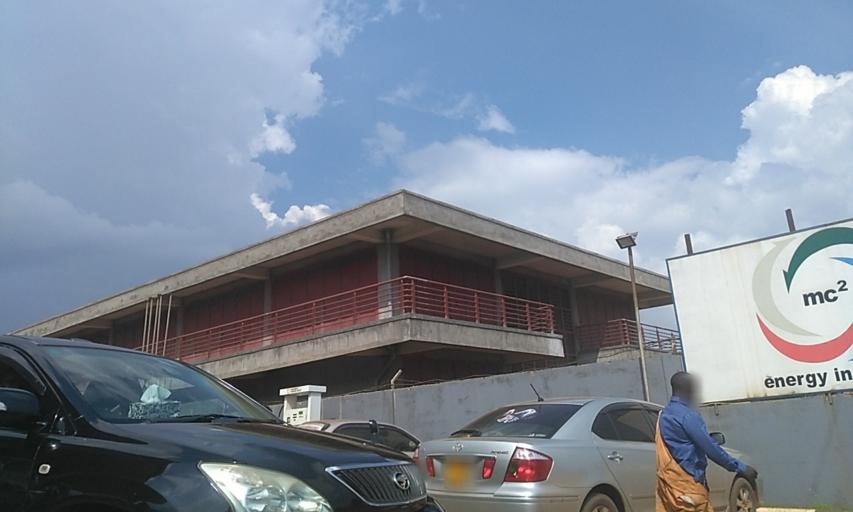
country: UG
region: Central Region
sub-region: Kampala District
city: Kampala
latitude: 0.2944
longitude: 32.5579
